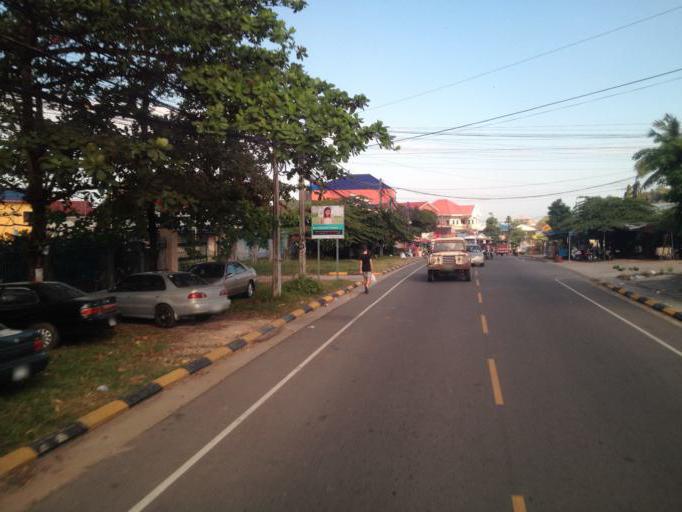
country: KH
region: Preah Sihanouk
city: Sihanoukville
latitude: 10.6329
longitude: 103.5050
